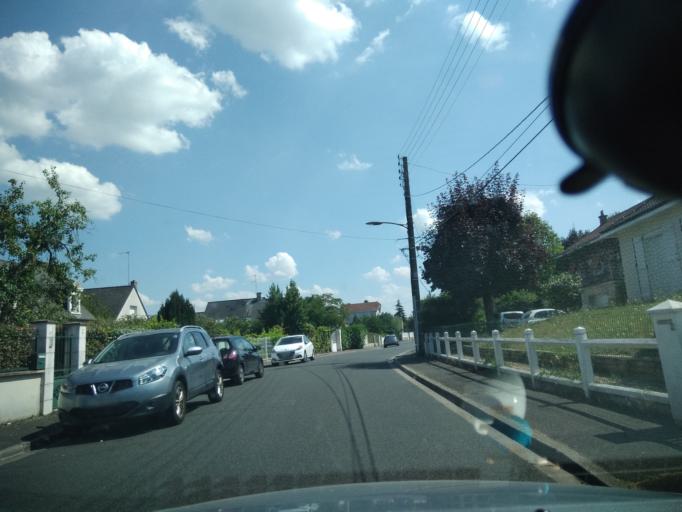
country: FR
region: Centre
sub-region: Departement d'Indre-et-Loire
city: Chambray-les-Tours
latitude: 47.3532
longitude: 0.6932
